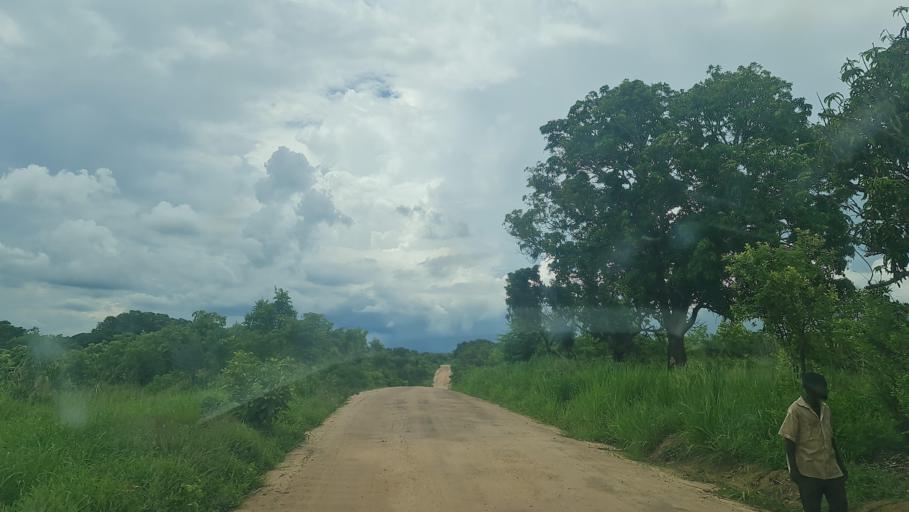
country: MW
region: Southern Region
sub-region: Nsanje District
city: Nsanje
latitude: -17.5919
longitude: 35.6741
